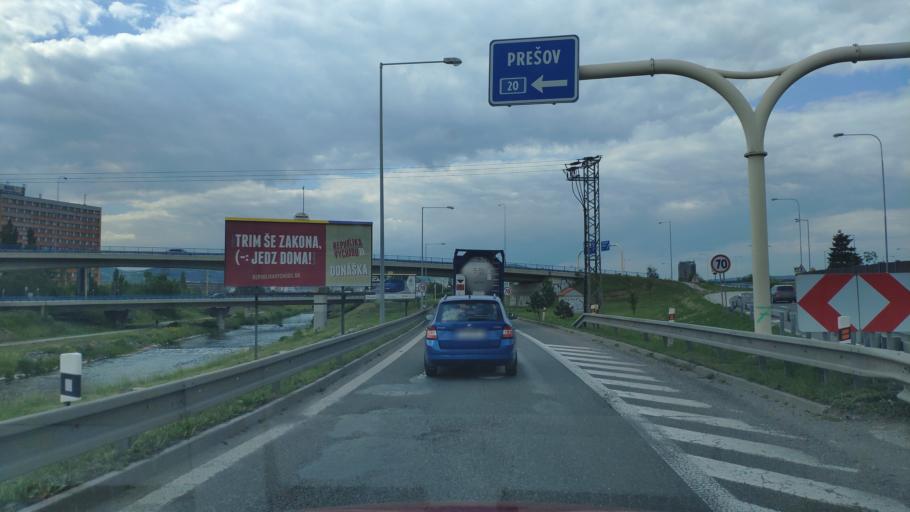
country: SK
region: Kosicky
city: Kosice
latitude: 48.7215
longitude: 21.2765
